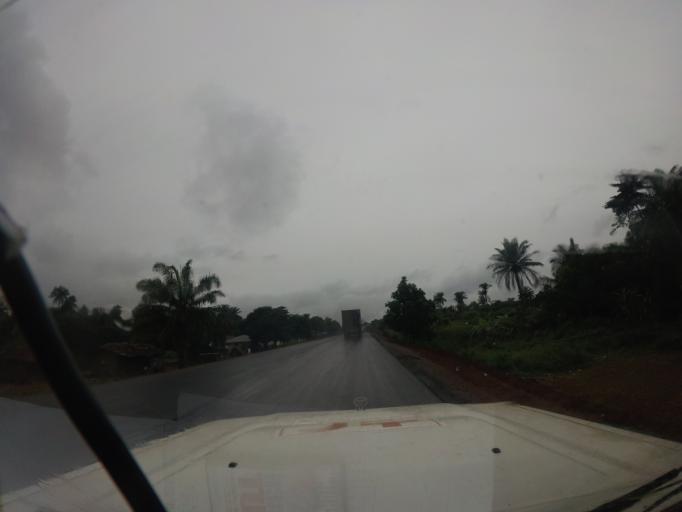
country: SL
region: Eastern Province
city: Tefeya
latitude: 8.5792
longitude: -11.3611
